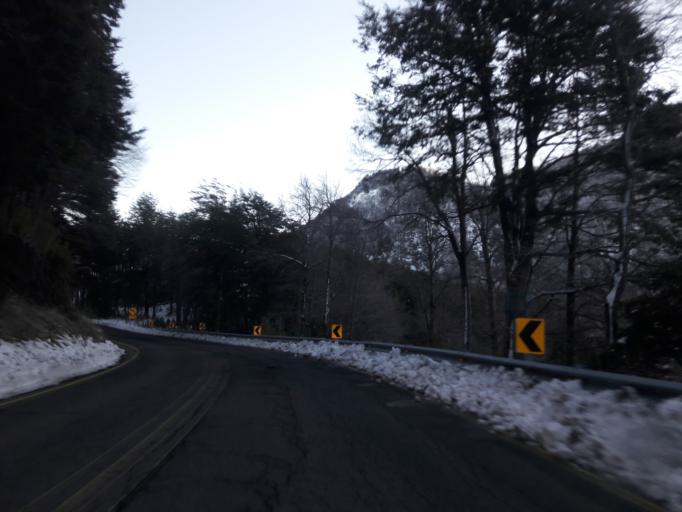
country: CL
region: Araucania
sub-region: Provincia de Cautin
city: Vilcun
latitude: -38.5038
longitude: -71.5200
